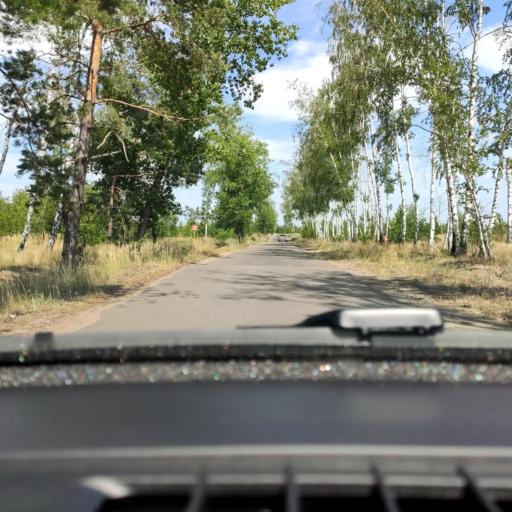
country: RU
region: Voronezj
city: Somovo
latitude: 51.7642
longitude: 39.3108
